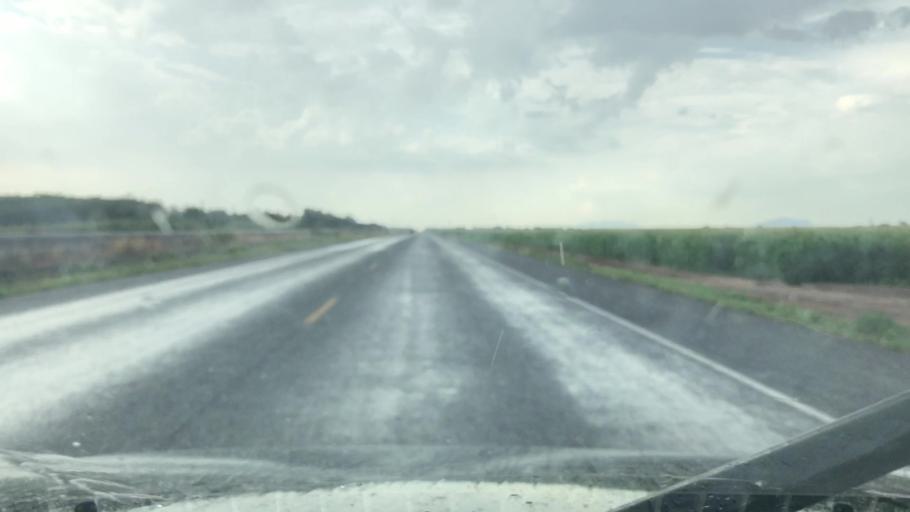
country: US
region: New Mexico
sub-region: Dona Ana County
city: Mesquite
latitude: 32.1390
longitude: -106.6804
